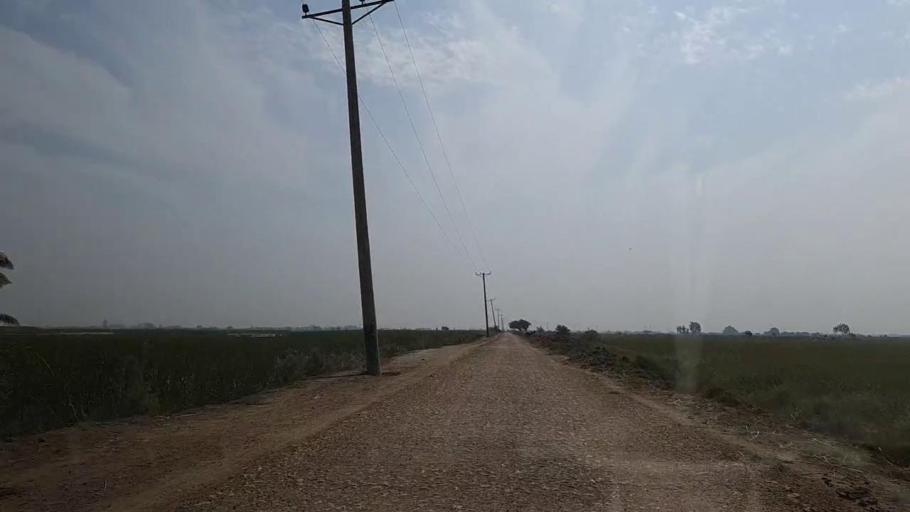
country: PK
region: Sindh
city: Mirpur Batoro
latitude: 24.6048
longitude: 68.2116
